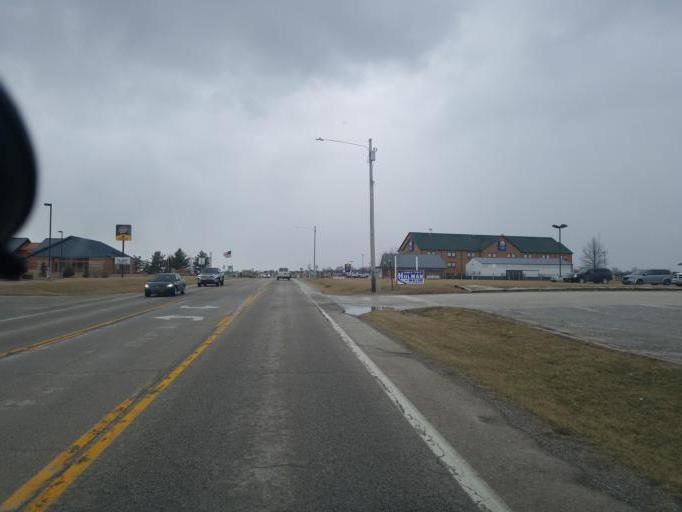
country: US
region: Missouri
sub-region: Macon County
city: Macon
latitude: 39.7595
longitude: -92.4676
